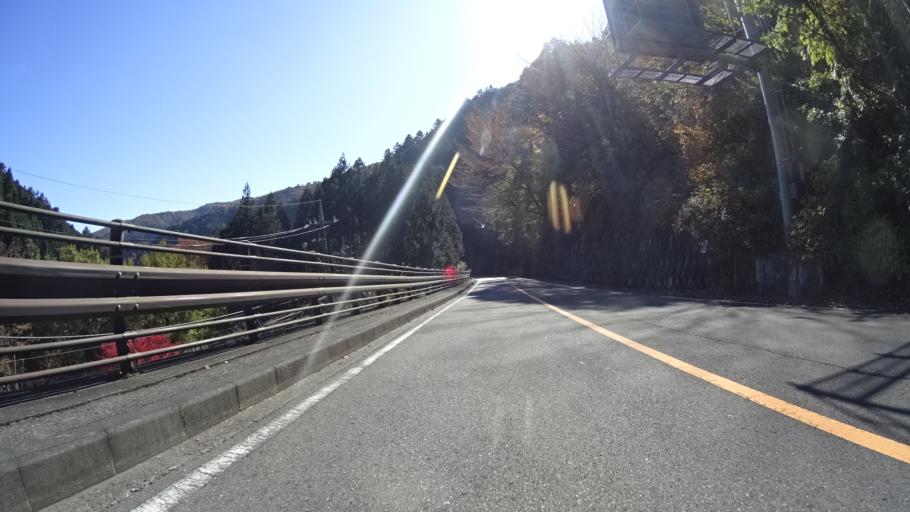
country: JP
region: Yamanashi
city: Uenohara
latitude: 35.7317
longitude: 139.0402
